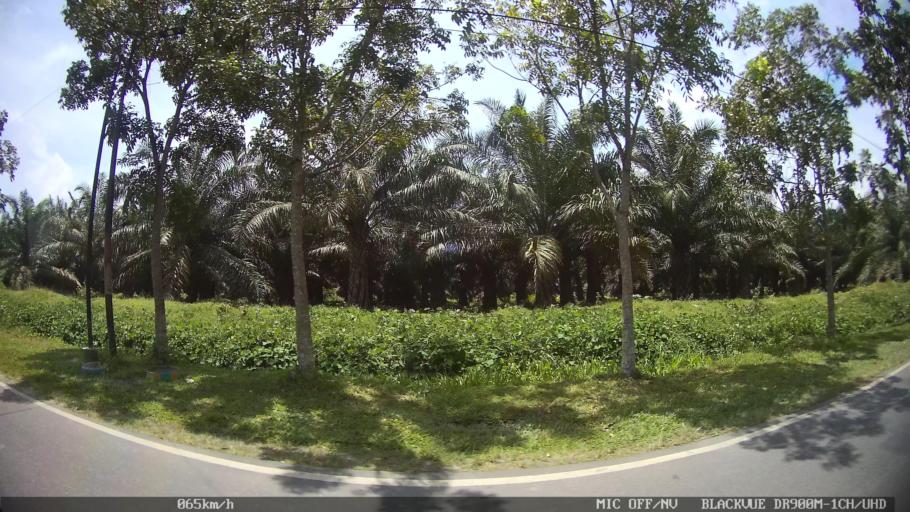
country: ID
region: North Sumatra
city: Percut
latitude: 3.5450
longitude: 98.8680
